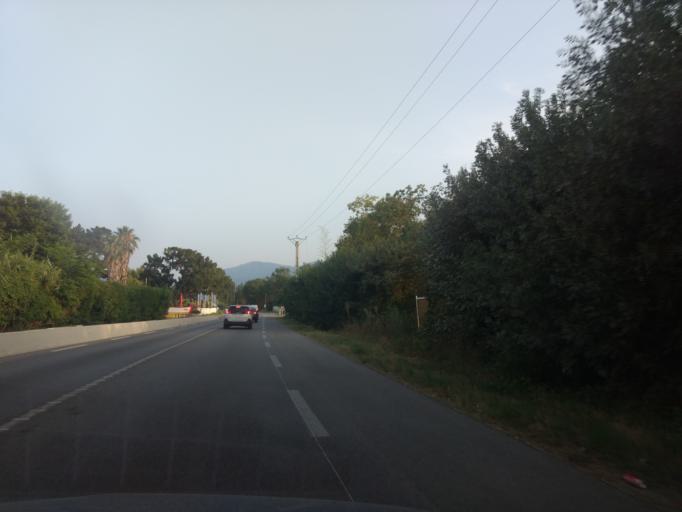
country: FR
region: Languedoc-Roussillon
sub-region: Departement des Pyrenees-Orientales
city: Argelers
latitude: 42.5815
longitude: 3.0326
